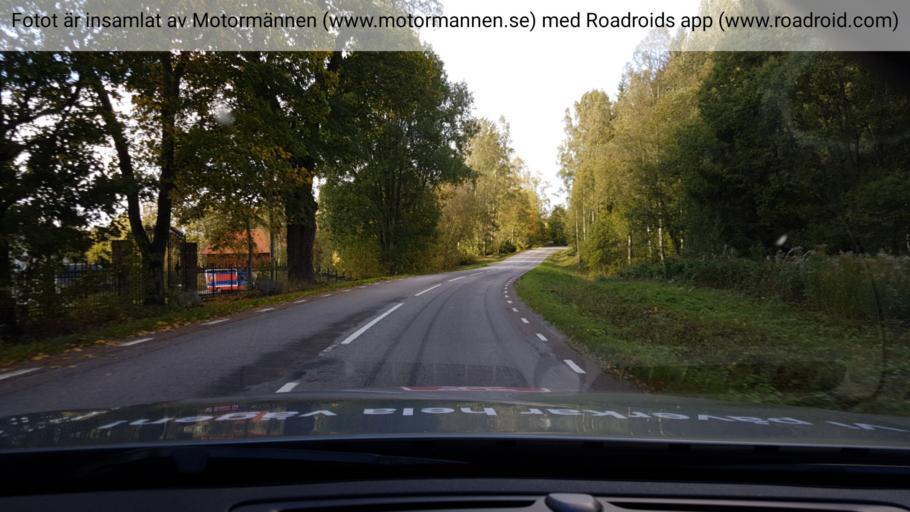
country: SE
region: Vaermland
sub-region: Filipstads Kommun
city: Filipstad
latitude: 59.7291
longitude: 14.1652
